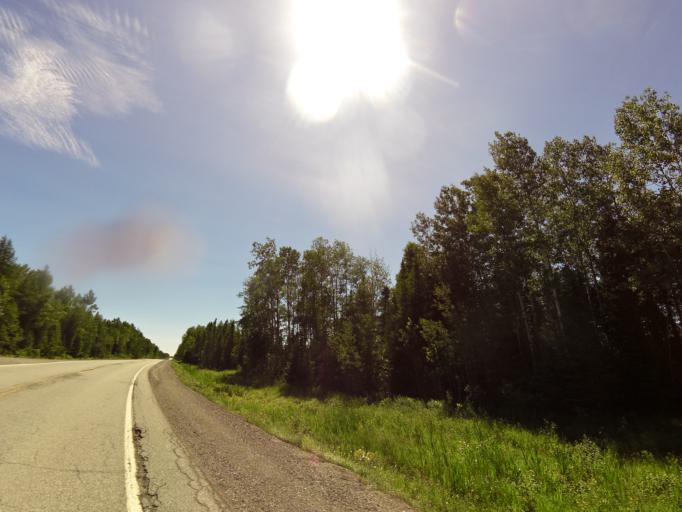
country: CA
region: Quebec
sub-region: Nord-du-Quebec
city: Lebel-sur-Quevillon
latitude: 48.8361
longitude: -77.1110
